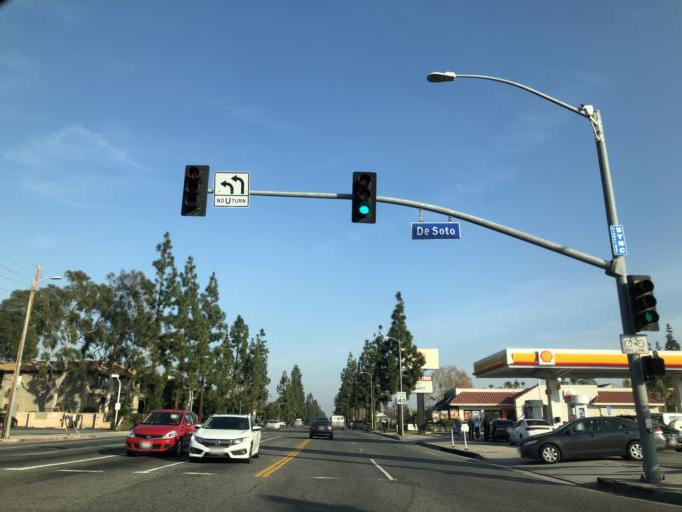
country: US
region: California
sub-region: Los Angeles County
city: Chatsworth
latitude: 34.2572
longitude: -118.5886
